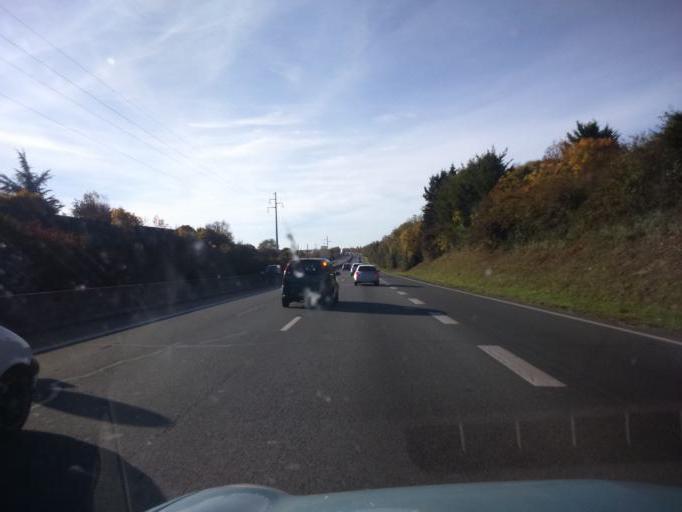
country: FR
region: Poitou-Charentes
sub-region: Departement de la Charente-Maritime
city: Puilboreau
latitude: 46.1689
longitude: -1.1208
